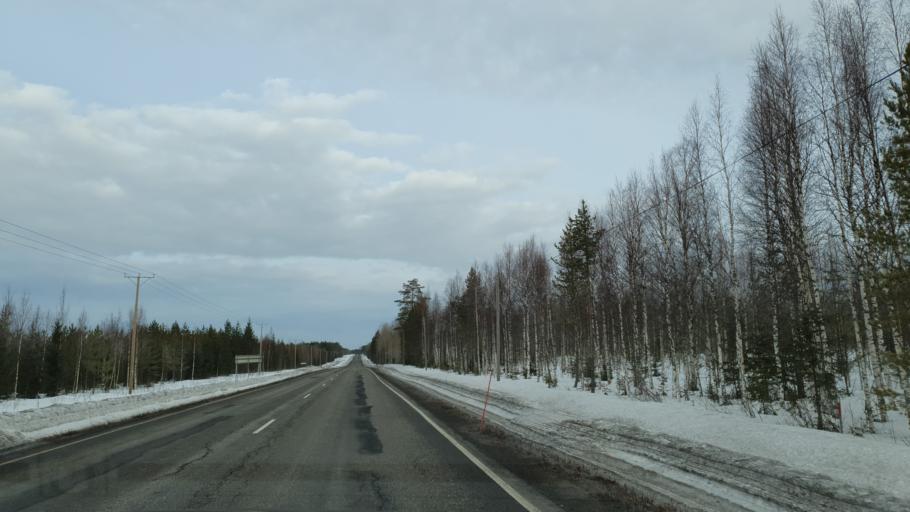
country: FI
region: Kainuu
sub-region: Kajaani
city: Vuokatti
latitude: 64.2056
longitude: 28.1514
